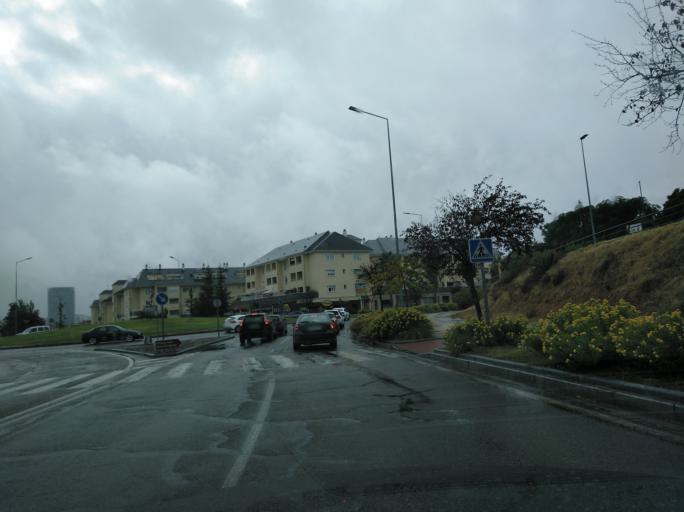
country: ES
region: Extremadura
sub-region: Provincia de Badajoz
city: Badajoz
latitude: 38.8840
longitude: -6.9912
